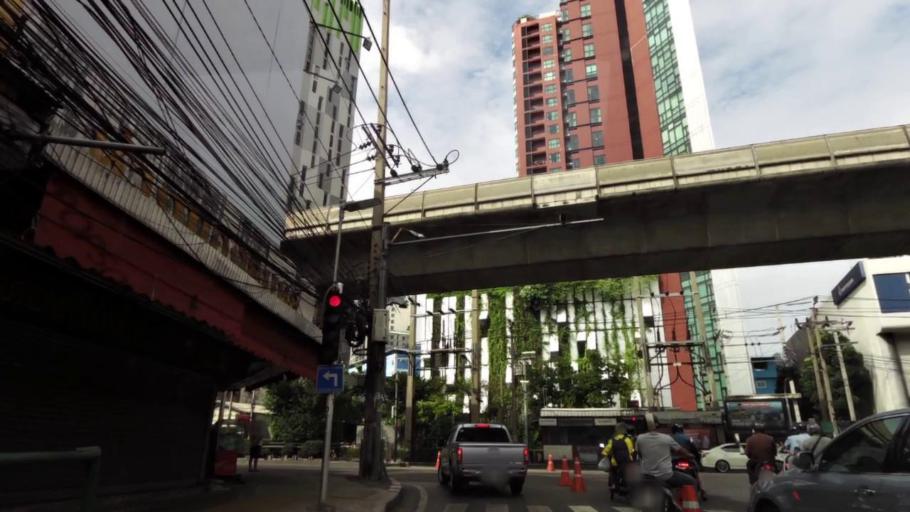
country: TH
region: Bangkok
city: Phra Khanong
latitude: 13.7134
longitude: 100.5943
